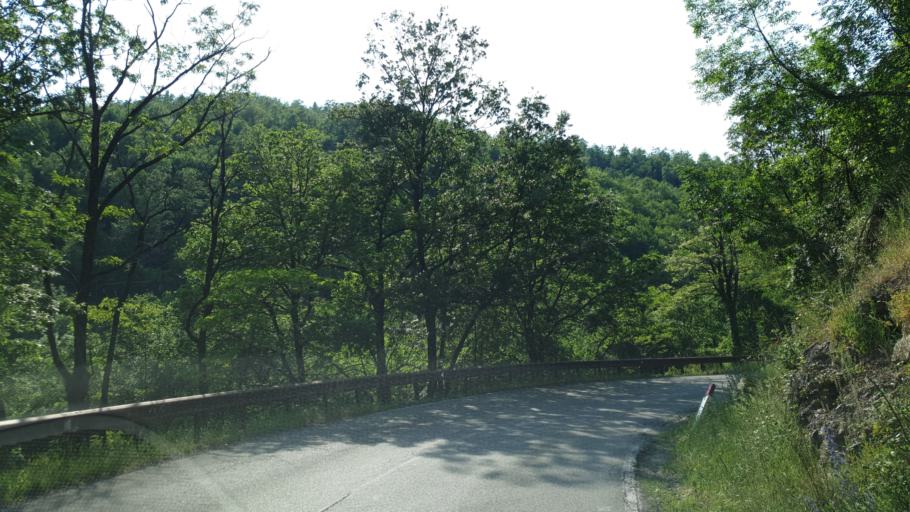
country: IT
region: Tuscany
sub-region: Province of Arezzo
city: Soci
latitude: 43.7667
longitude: 11.8378
